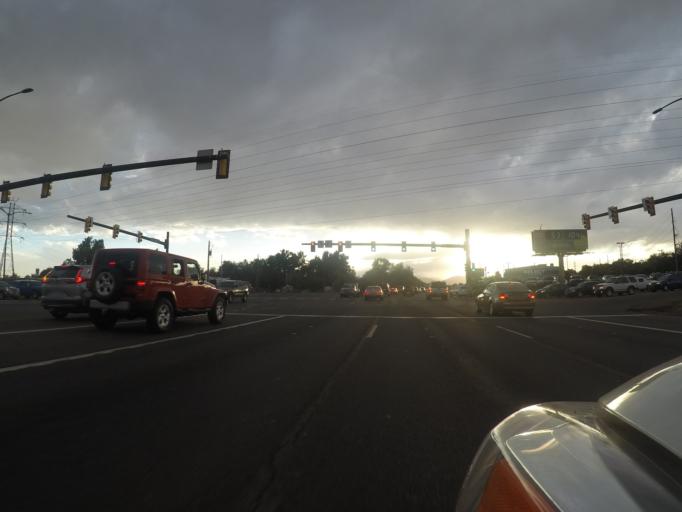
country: US
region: Colorado
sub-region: Arapahoe County
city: Sheridan
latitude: 39.6533
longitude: -105.0136
